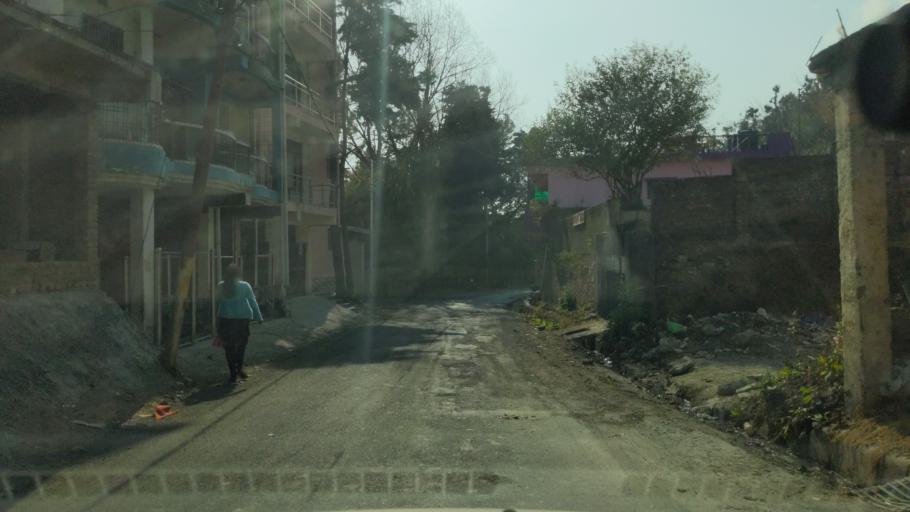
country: IN
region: Uttarakhand
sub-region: Naini Tal
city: Bhowali
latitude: 29.3859
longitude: 79.5287
